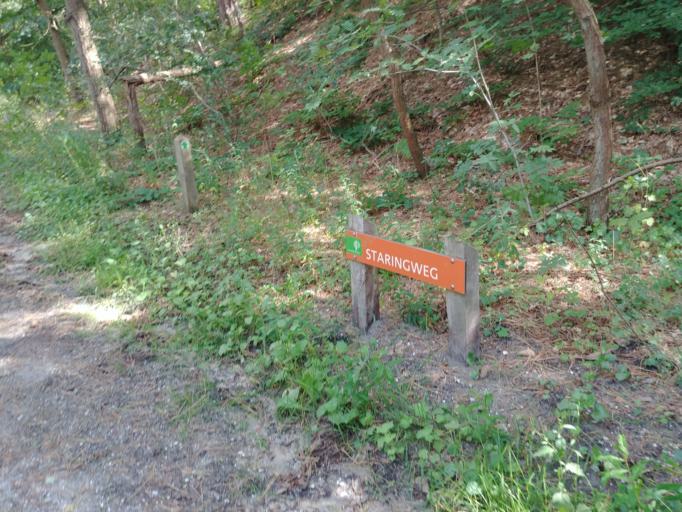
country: NL
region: North Holland
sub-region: Gemeente Alkmaar
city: Alkmaar
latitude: 52.6892
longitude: 4.6897
